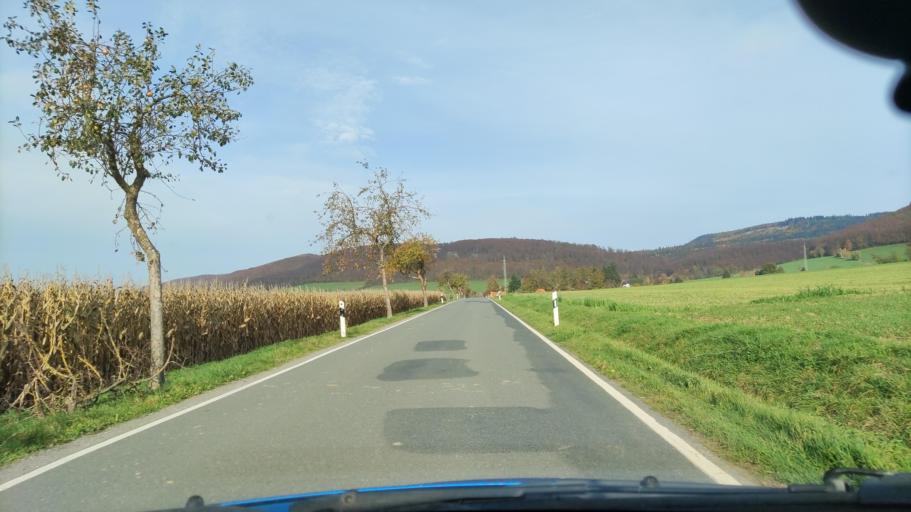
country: DE
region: Lower Saxony
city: Holzen
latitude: 51.9259
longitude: 9.6655
